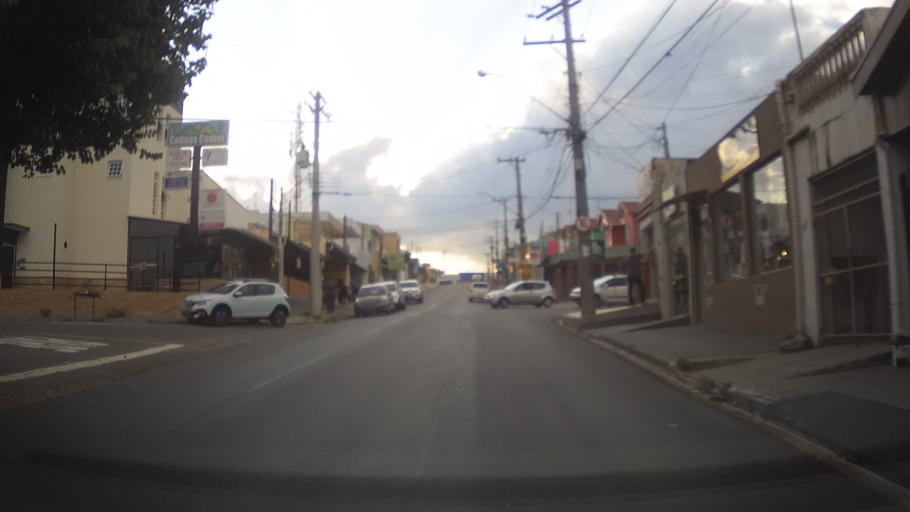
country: BR
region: Sao Paulo
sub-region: Jundiai
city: Jundiai
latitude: -23.1870
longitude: -46.9638
